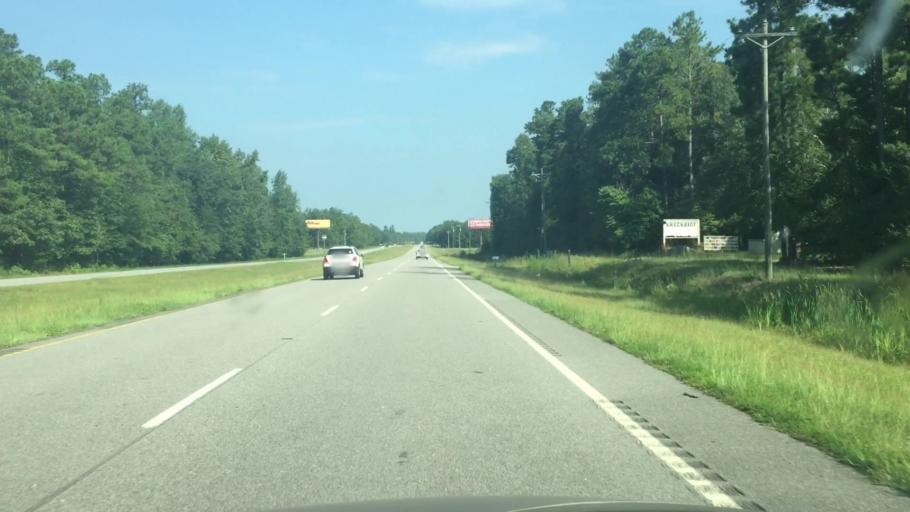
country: US
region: South Carolina
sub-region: Horry County
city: Loris
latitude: 34.0568
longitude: -78.8439
